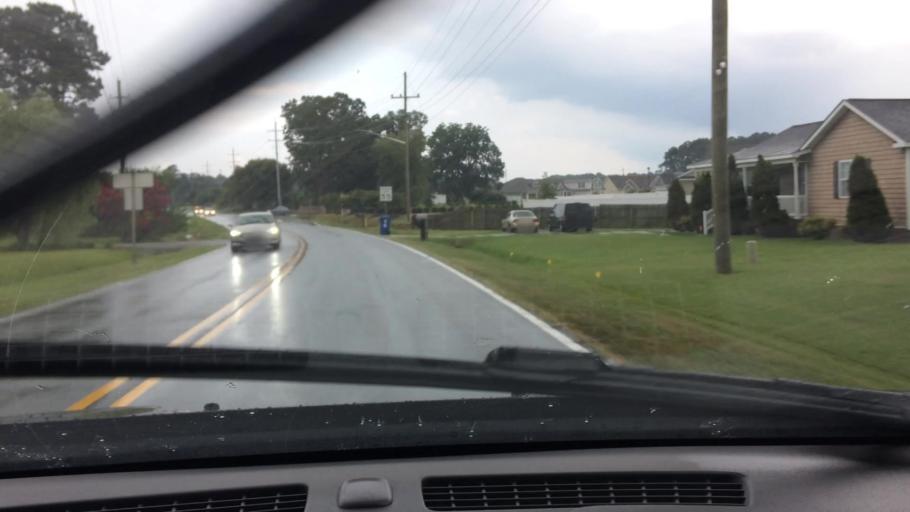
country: US
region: North Carolina
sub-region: Pitt County
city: Winterville
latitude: 35.5212
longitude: -77.3851
